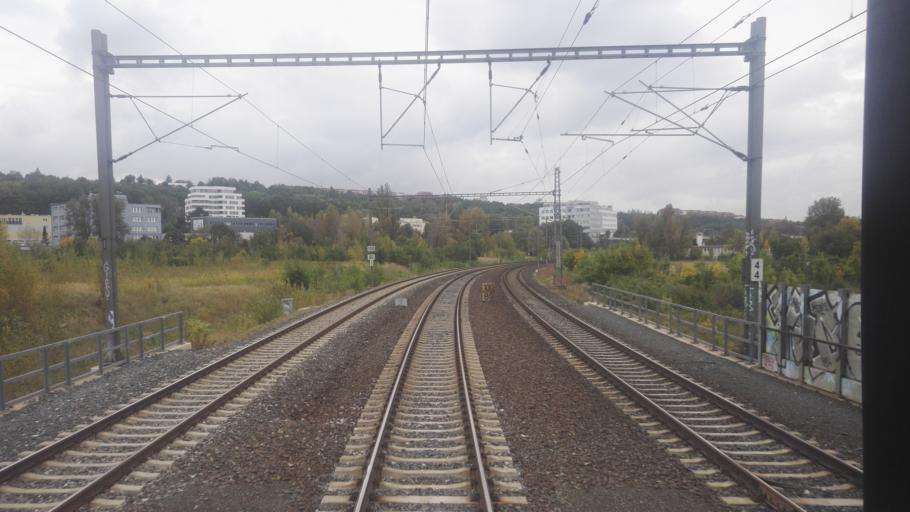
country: CZ
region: Praha
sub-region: Praha 8
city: Liben
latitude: 50.1013
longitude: 14.4803
